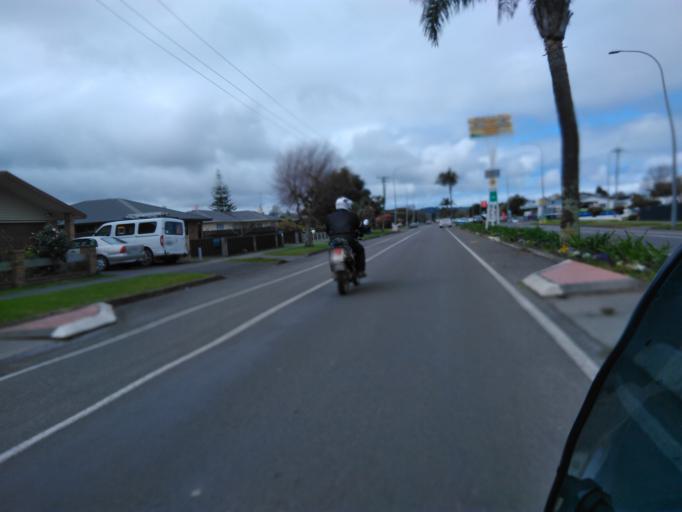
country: NZ
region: Gisborne
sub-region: Gisborne District
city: Gisborne
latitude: -38.6500
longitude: 177.9901
